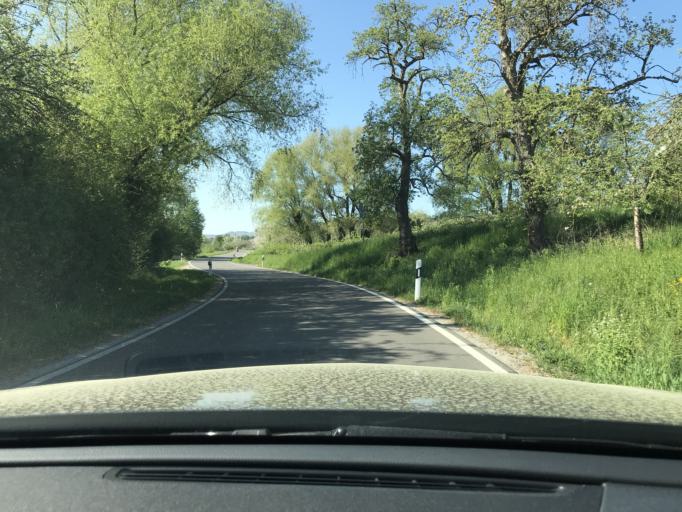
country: DE
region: Baden-Wuerttemberg
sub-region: Regierungsbezirk Stuttgart
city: Baltmannsweiler
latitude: 48.7782
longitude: 9.4134
